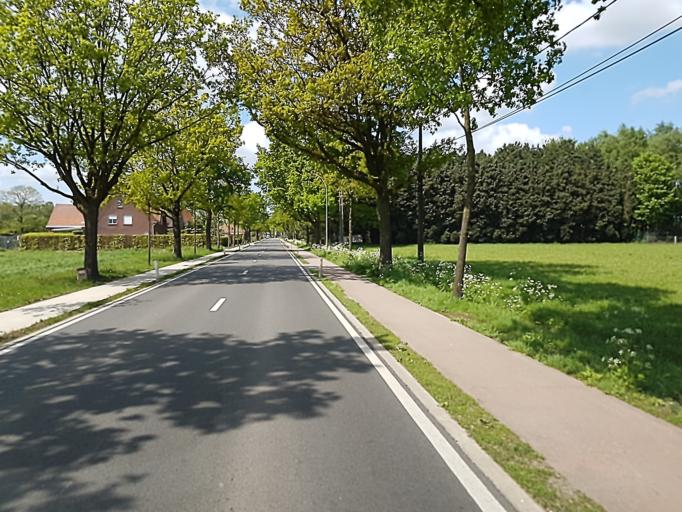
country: BE
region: Flanders
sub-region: Provincie Antwerpen
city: Rijkevorsel
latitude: 51.3489
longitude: 4.7288
